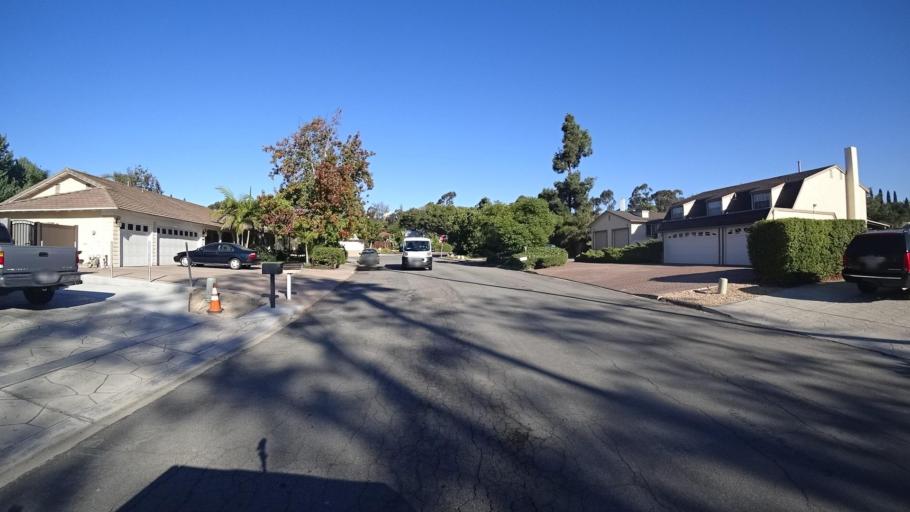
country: US
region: California
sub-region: San Diego County
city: Bonita
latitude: 32.6824
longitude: -117.0251
